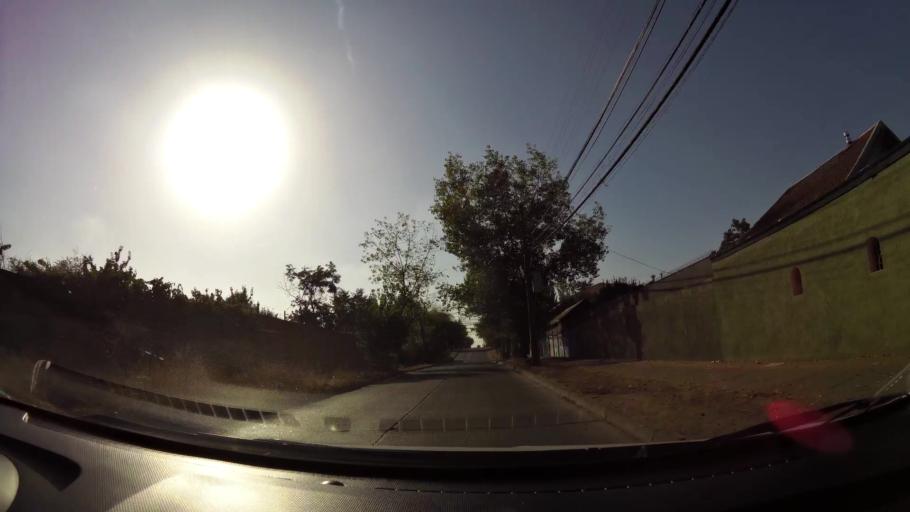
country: CL
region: Maule
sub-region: Provincia de Talca
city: Talca
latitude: -35.4079
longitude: -71.6563
